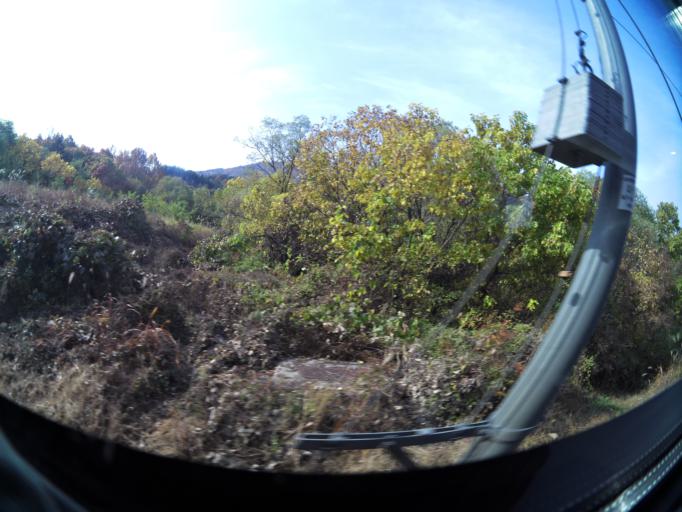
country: KR
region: Gyeongsangbuk-do
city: Gimcheon
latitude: 36.1885
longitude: 128.0072
